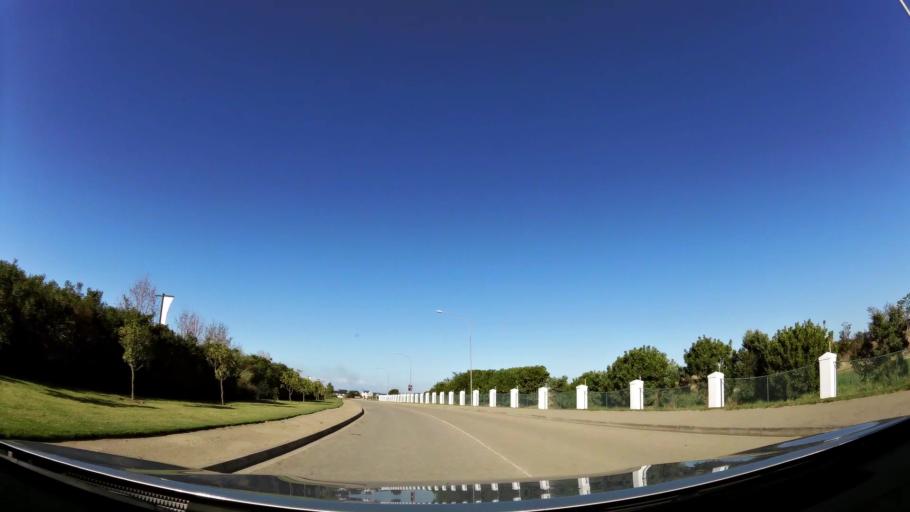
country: ZA
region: Western Cape
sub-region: Eden District Municipality
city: George
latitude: -33.9668
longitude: 22.4294
